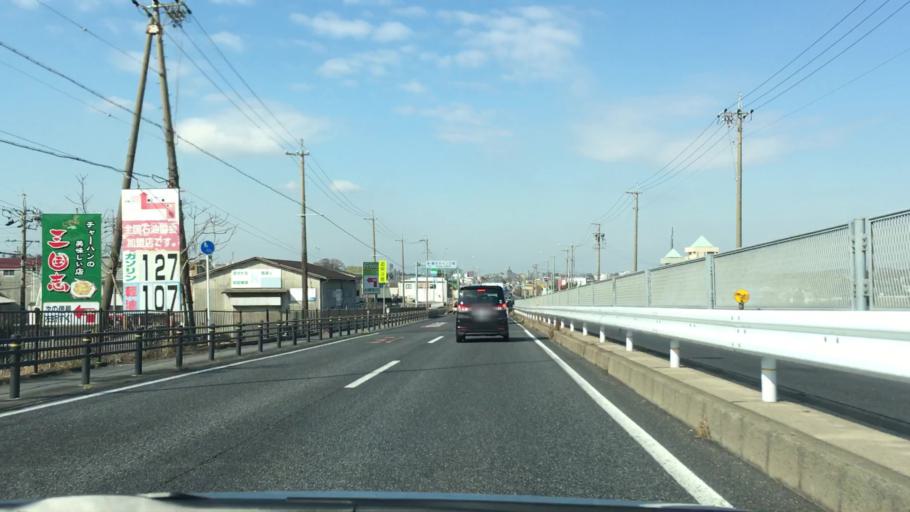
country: JP
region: Aichi
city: Okazaki
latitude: 34.9242
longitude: 137.2029
